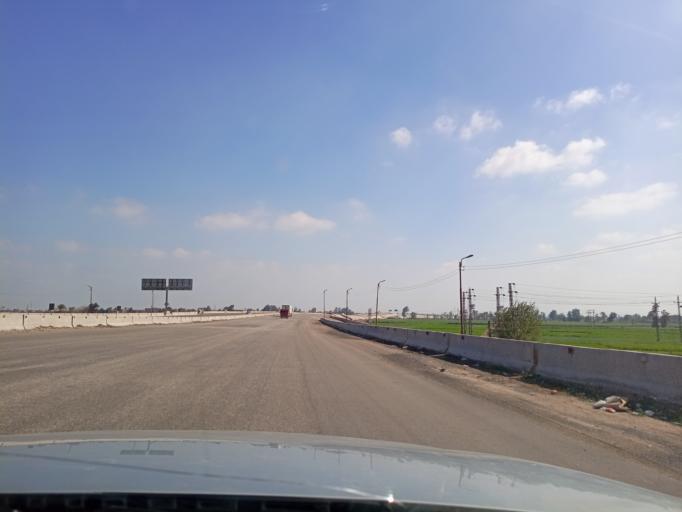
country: EG
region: Eastern Province
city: Mashtul as Suq
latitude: 30.4628
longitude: 31.3702
